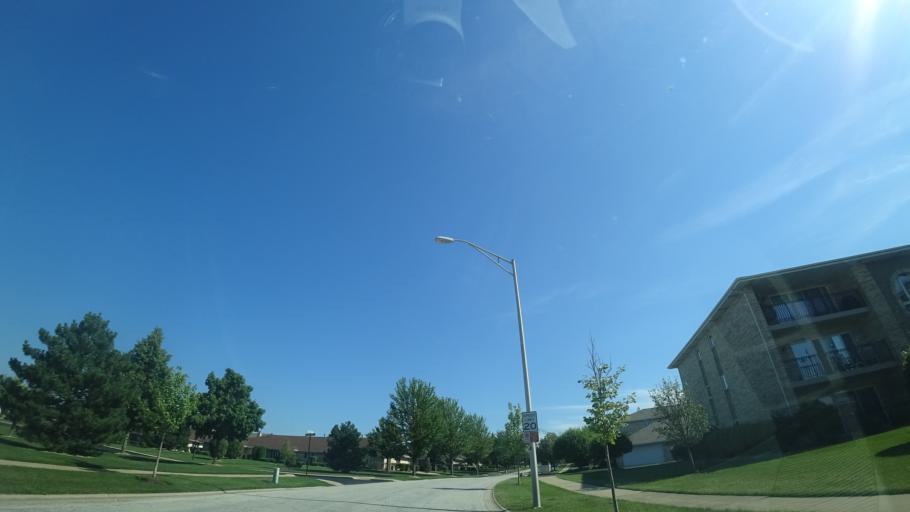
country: US
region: Illinois
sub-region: Will County
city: Mokena
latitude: 41.5671
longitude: -87.8869
